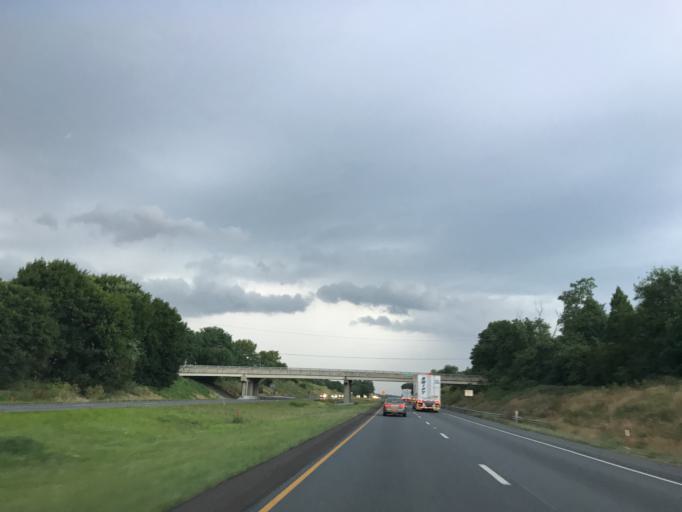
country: US
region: Pennsylvania
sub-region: Lancaster County
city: Brownstown
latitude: 40.0906
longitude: -76.2637
